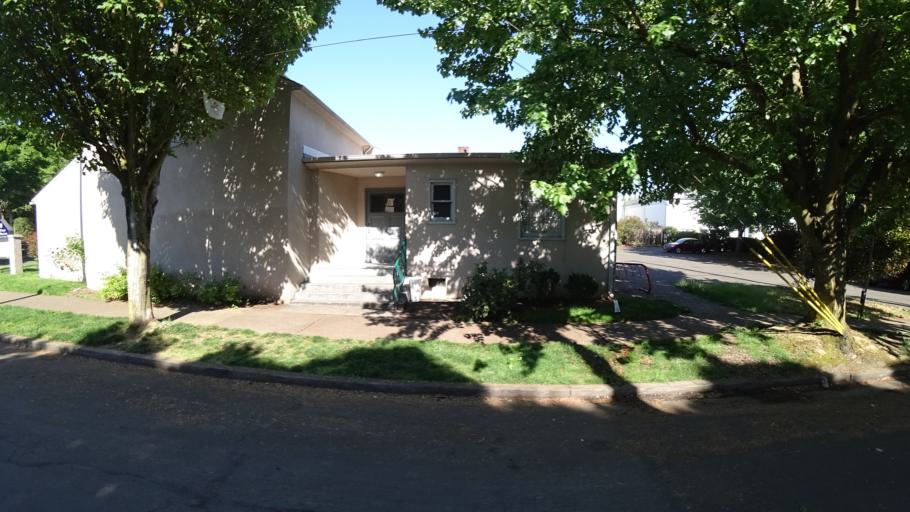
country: US
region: Oregon
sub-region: Multnomah County
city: Portland
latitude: 45.5416
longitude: -122.6641
